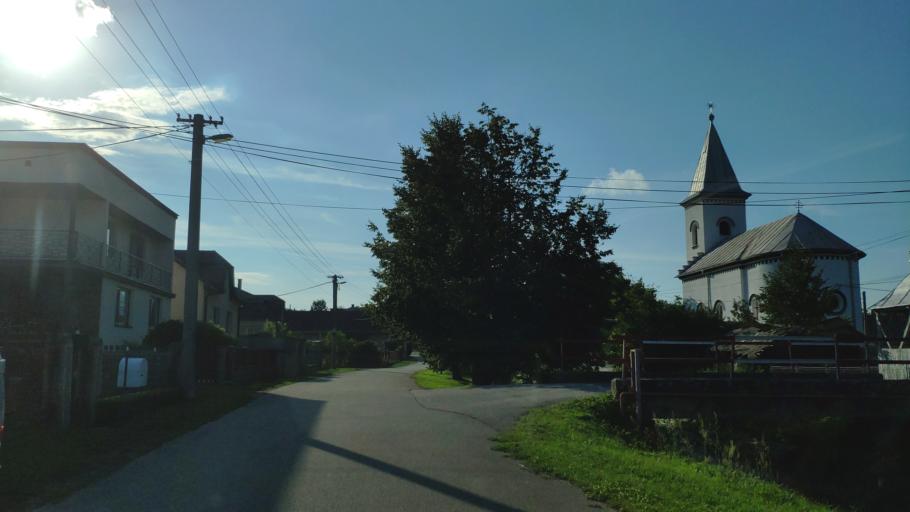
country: SK
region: Kosicky
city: Secovce
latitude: 48.6124
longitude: 21.5262
